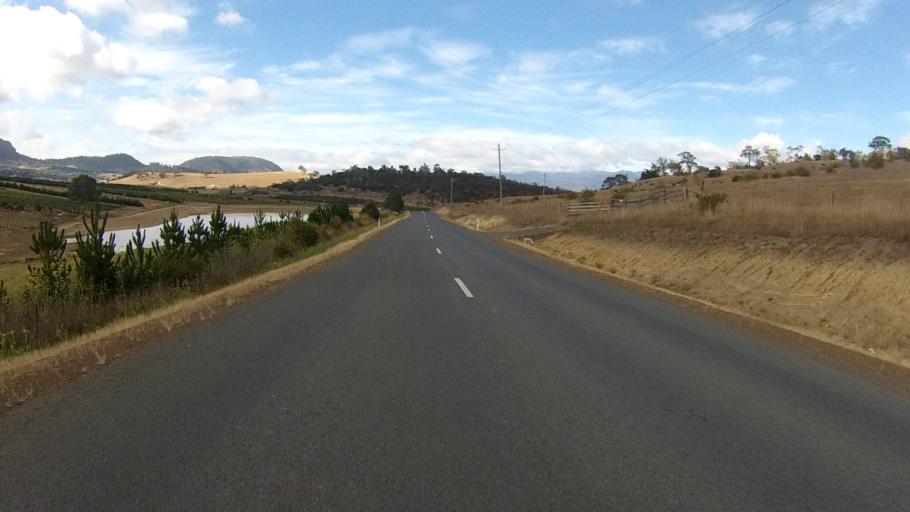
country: AU
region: Tasmania
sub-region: Brighton
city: Old Beach
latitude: -42.7373
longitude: 147.2884
